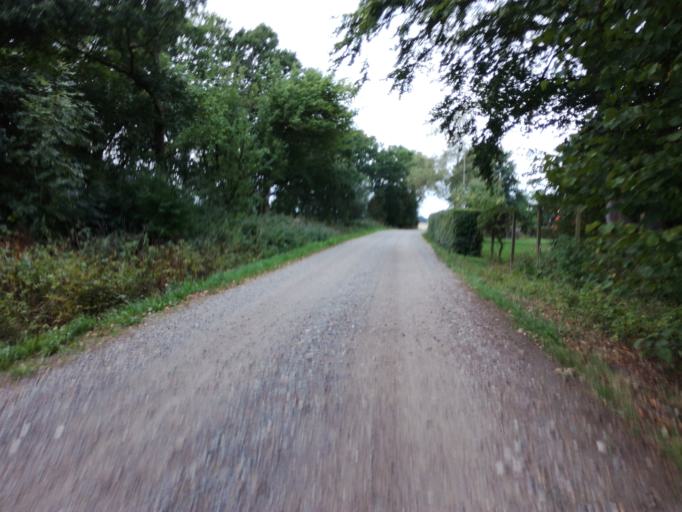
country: DK
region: South Denmark
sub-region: Fredericia Kommune
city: Fredericia
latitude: 55.5996
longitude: 9.7767
